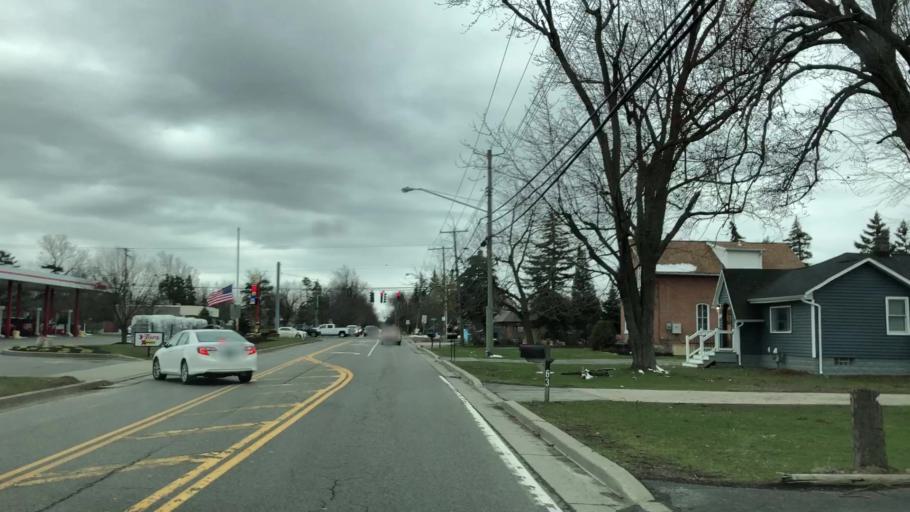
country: US
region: New York
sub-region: Erie County
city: Lancaster
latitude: 42.8817
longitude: -78.6768
